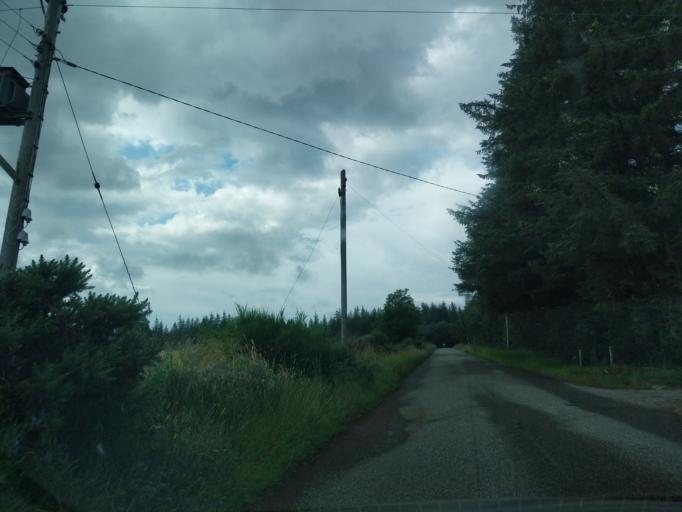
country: GB
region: Scotland
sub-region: Moray
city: Rothes
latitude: 57.4626
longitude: -3.2939
